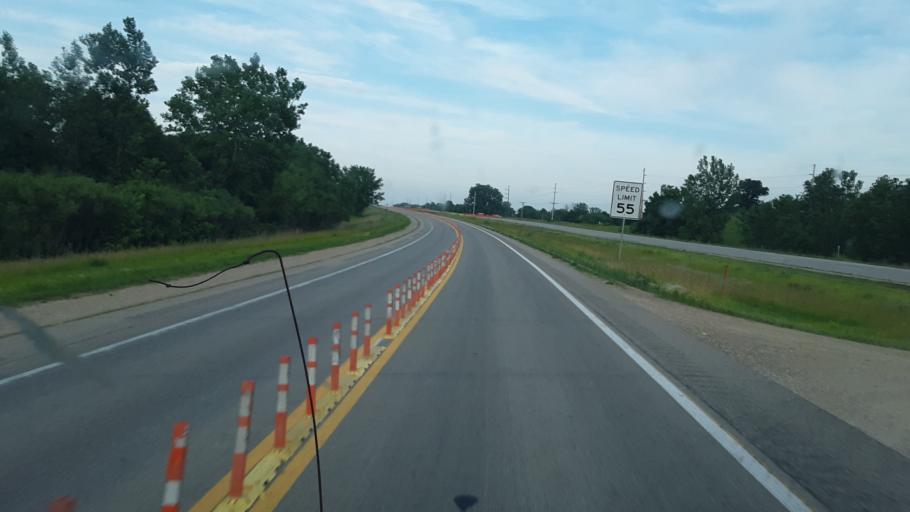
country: US
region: Iowa
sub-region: Tama County
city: Toledo
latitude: 42.0003
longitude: -92.7021
